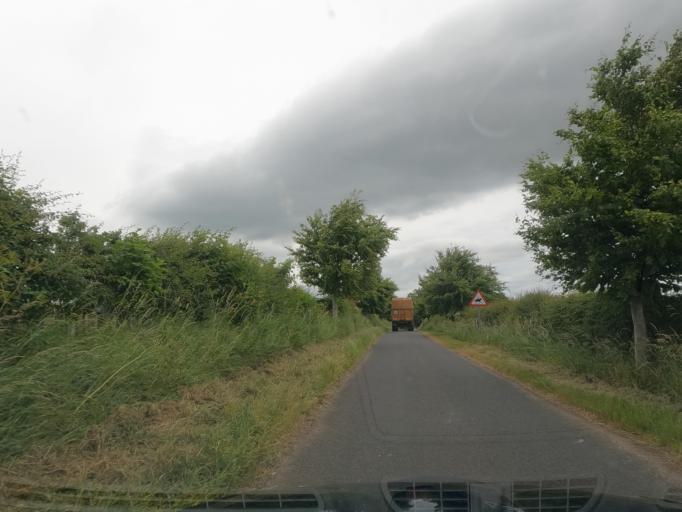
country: GB
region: England
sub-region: Northumberland
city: Lowick
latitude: 55.5826
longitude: -1.9223
